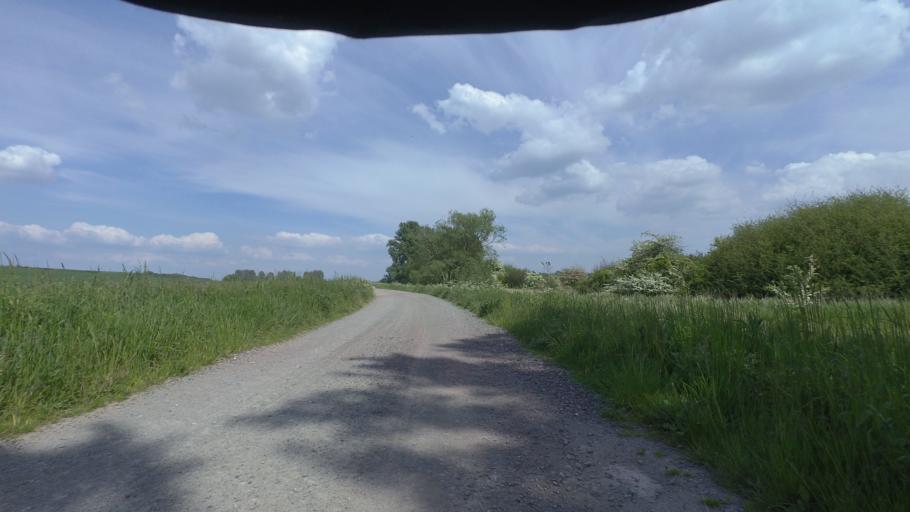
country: DE
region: Lower Saxony
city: Sollingen
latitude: 52.1046
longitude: 10.9490
